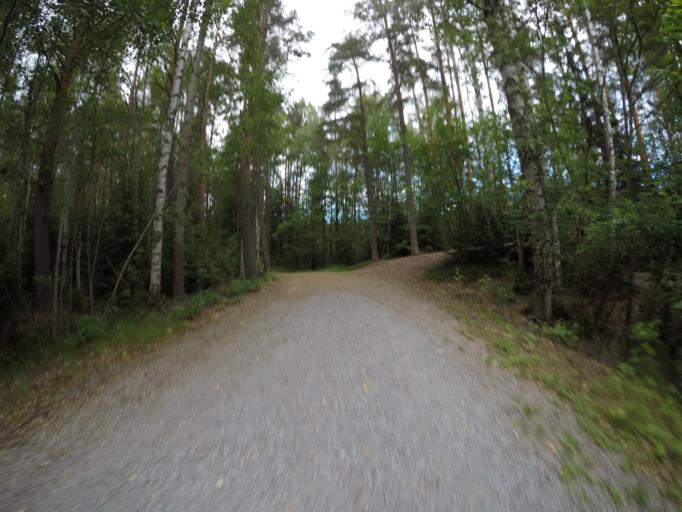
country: FI
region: Haeme
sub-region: Haemeenlinna
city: Haemeenlinna
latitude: 60.9964
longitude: 24.4142
